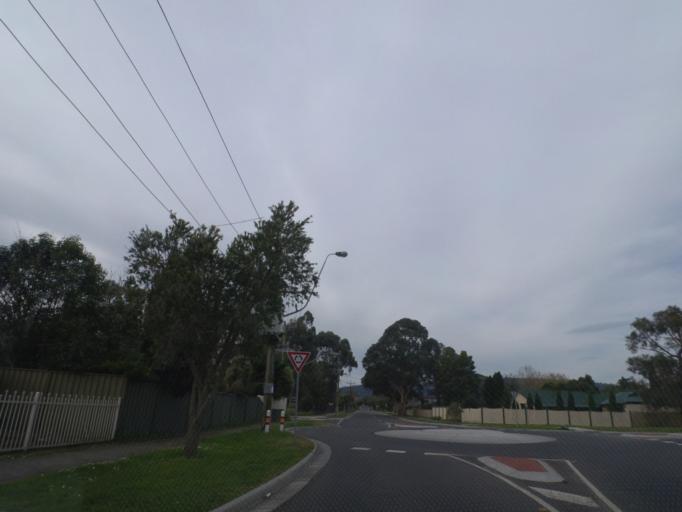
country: AU
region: Victoria
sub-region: Knox
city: Knoxfield
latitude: -37.8926
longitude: 145.2696
